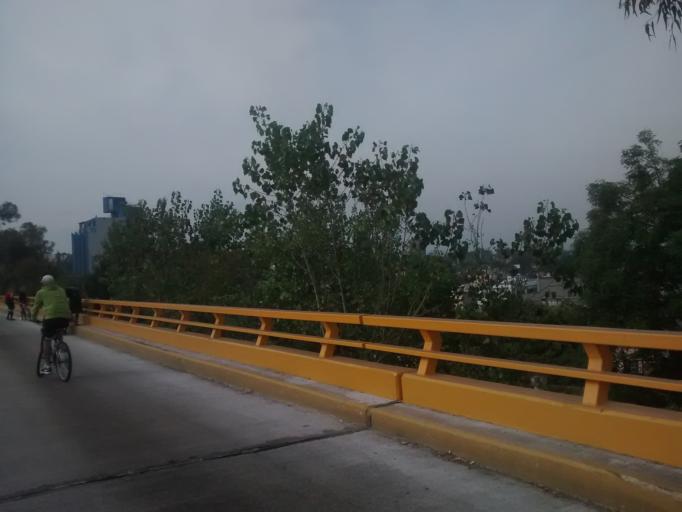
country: MX
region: Mexico City
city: Colonia Nativitas
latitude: 19.3598
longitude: -99.1306
